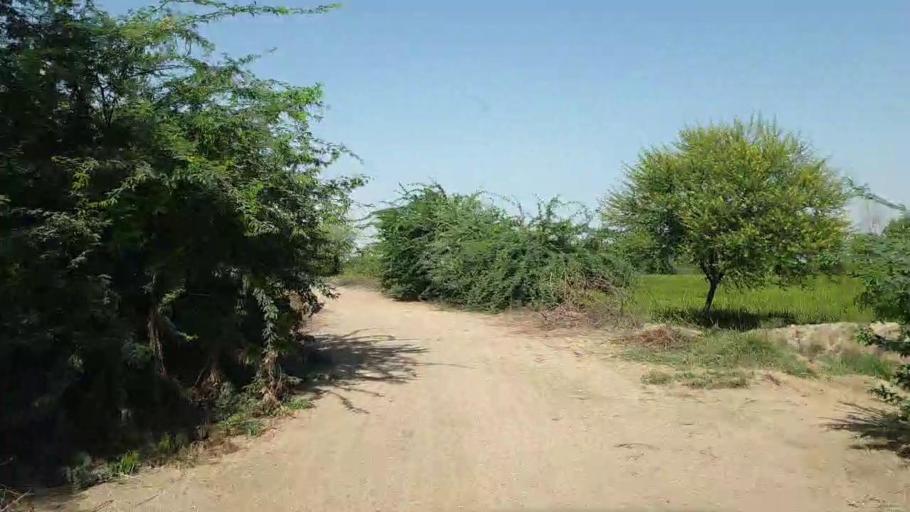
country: PK
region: Sindh
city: Tando Bago
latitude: 24.7412
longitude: 69.0433
